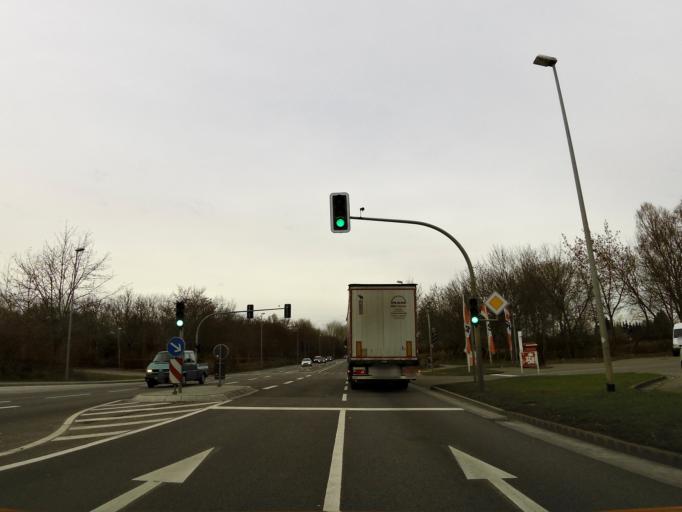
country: DE
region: Saxony-Anhalt
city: Salzwedel
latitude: 52.8444
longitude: 11.1668
